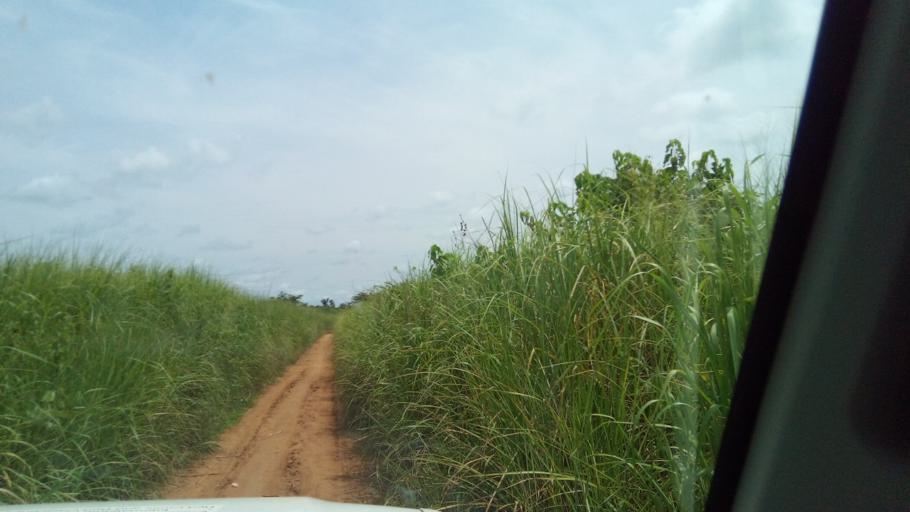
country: AO
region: Zaire
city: Mbanza Congo
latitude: -5.8041
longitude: 13.9958
